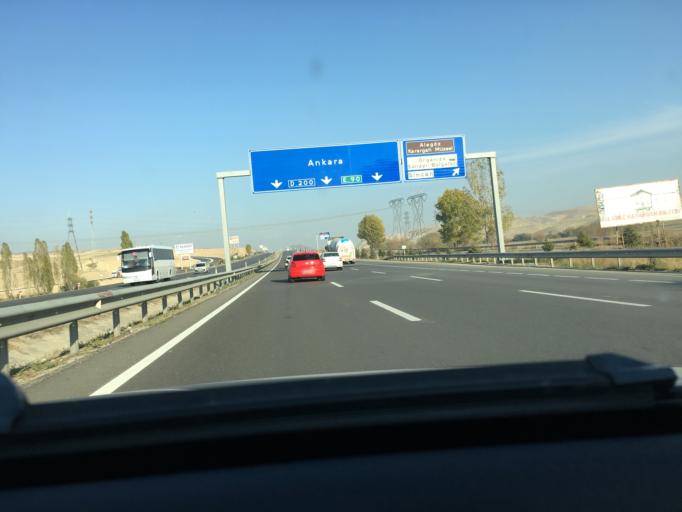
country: TR
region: Ankara
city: Temelli
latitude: 39.7550
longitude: 32.4453
